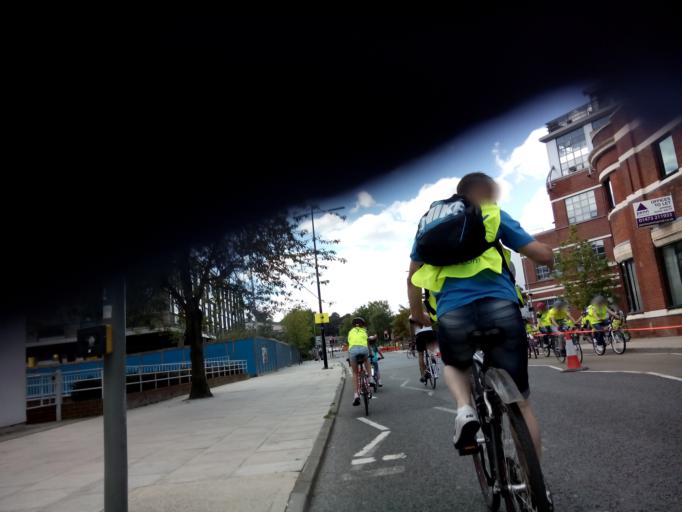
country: GB
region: England
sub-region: Suffolk
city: Ipswich
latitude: 52.0541
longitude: 1.1470
